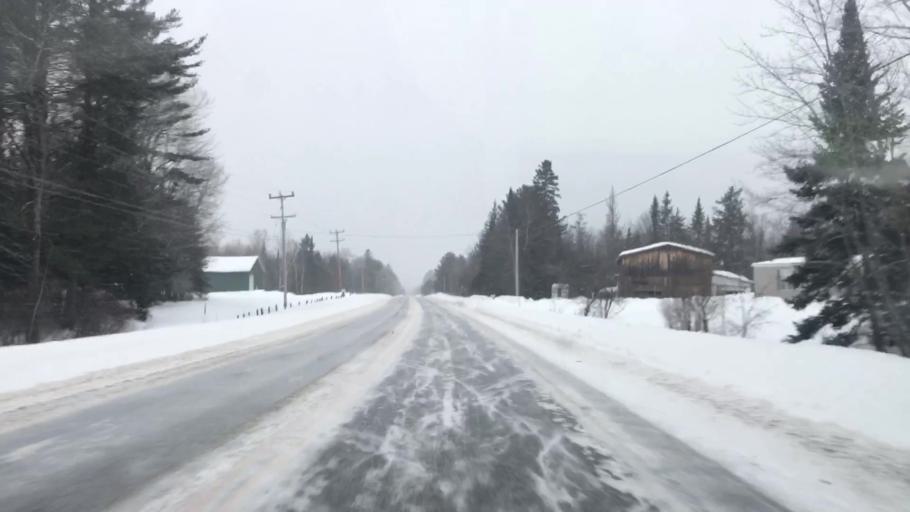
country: US
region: Maine
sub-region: Penobscot County
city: Medway
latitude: 45.5436
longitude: -68.3708
